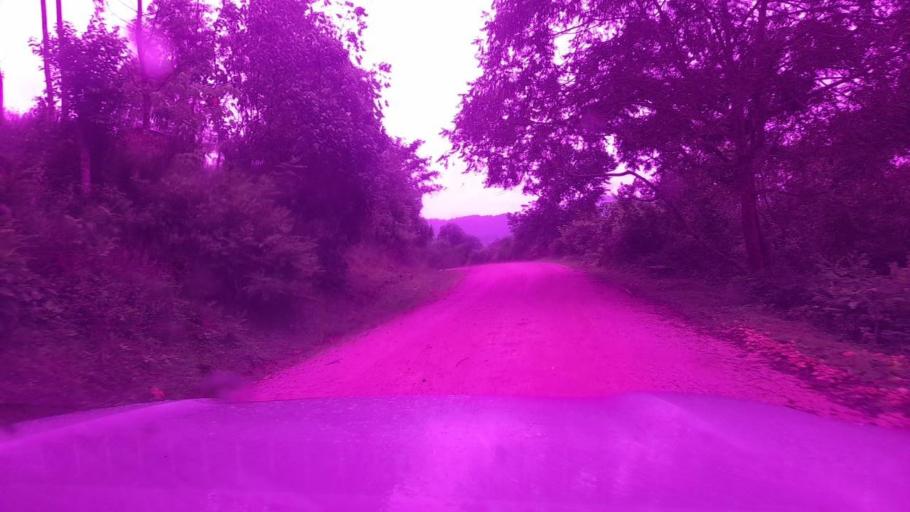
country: ET
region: Southern Nations, Nationalities, and People's Region
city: Bonga
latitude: 7.4517
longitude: 36.1288
